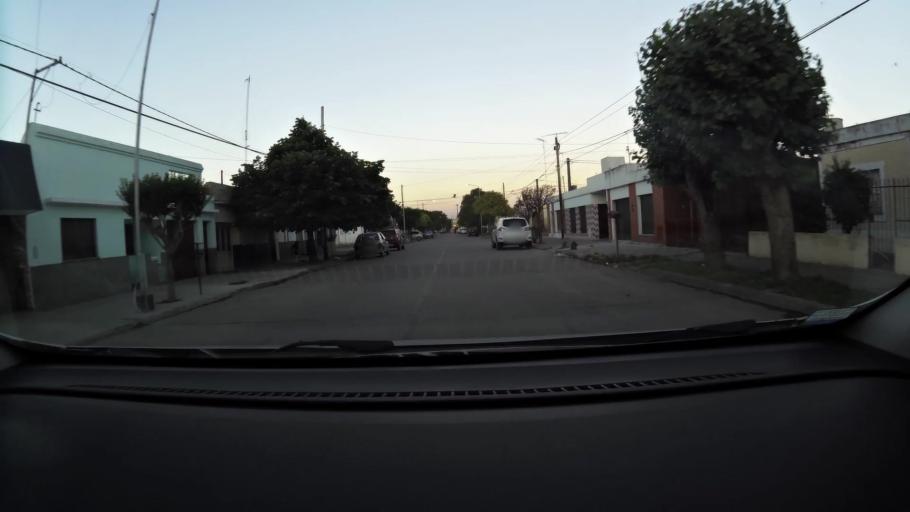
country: AR
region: Cordoba
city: Villa Maria
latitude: -32.4103
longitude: -63.2581
